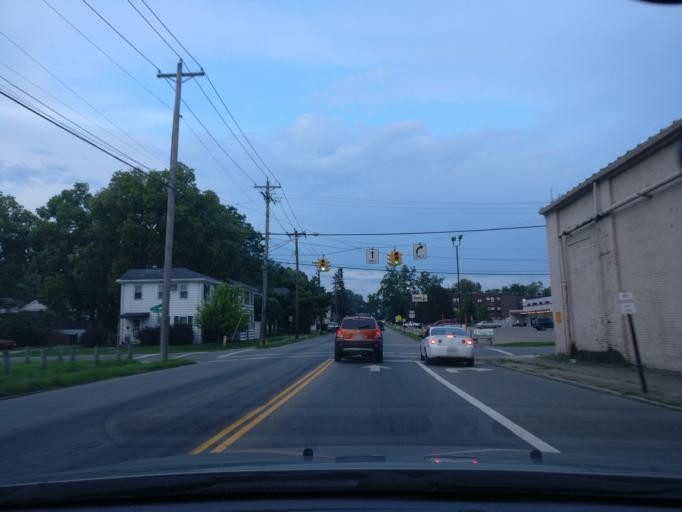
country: US
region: Ohio
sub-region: Warren County
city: Franklin
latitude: 39.5568
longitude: -84.3039
